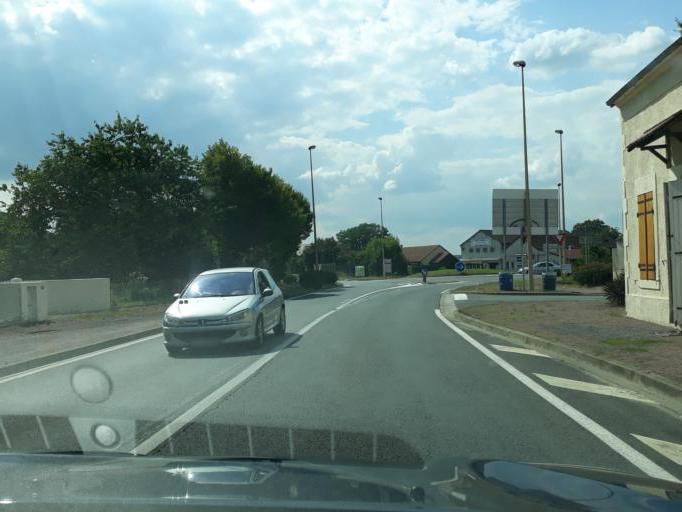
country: FR
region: Bourgogne
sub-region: Departement de la Nievre
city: Fourchambault
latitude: 47.0130
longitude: 3.0675
